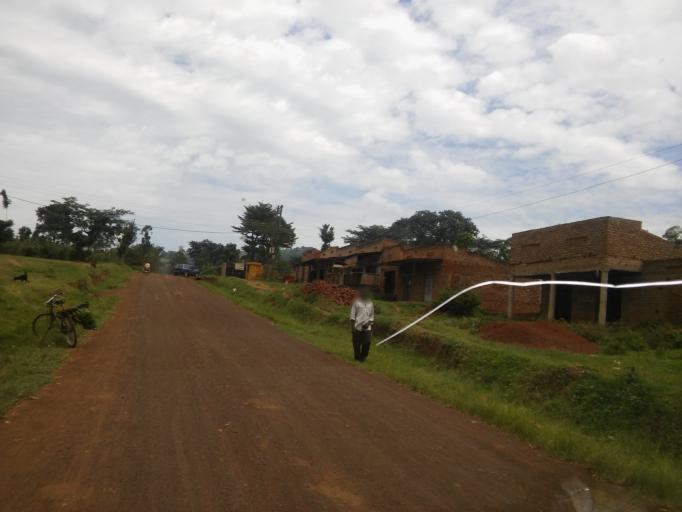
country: UG
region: Eastern Region
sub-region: Bududa District
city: Bududa
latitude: 0.9348
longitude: 34.2850
